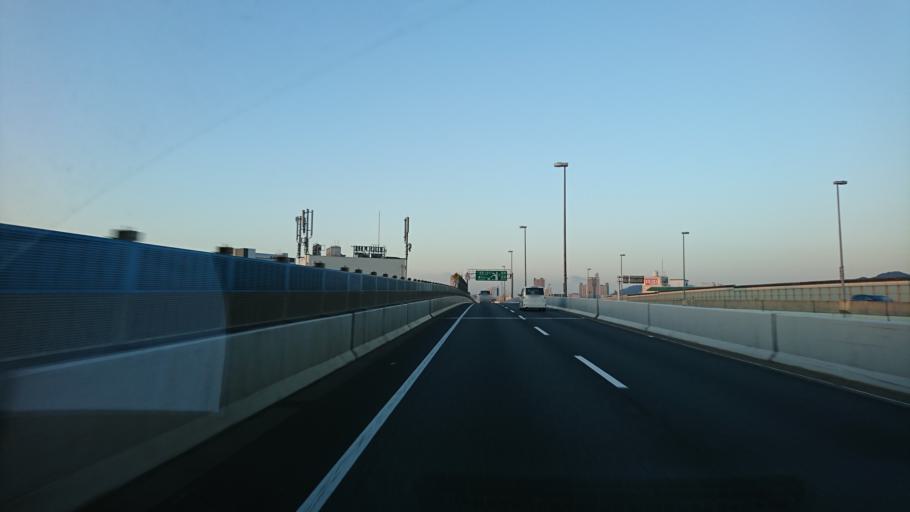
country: JP
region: Hyogo
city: Kobe
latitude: 34.6634
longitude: 135.1619
